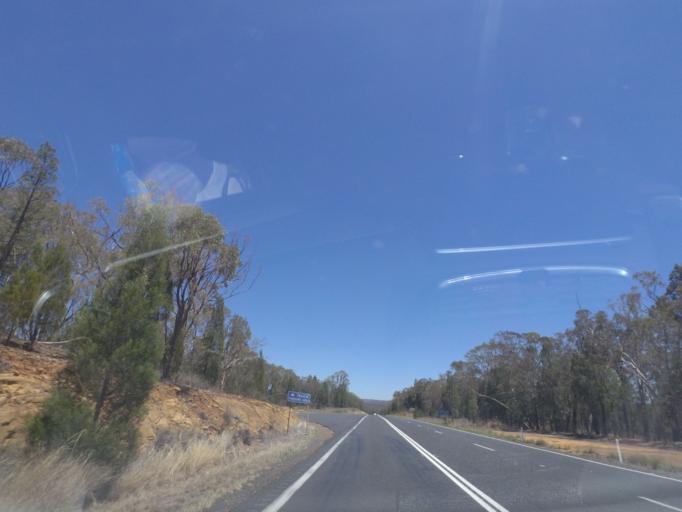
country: AU
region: New South Wales
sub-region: Warrumbungle Shire
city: Coonabarabran
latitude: -31.2337
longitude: 149.3176
